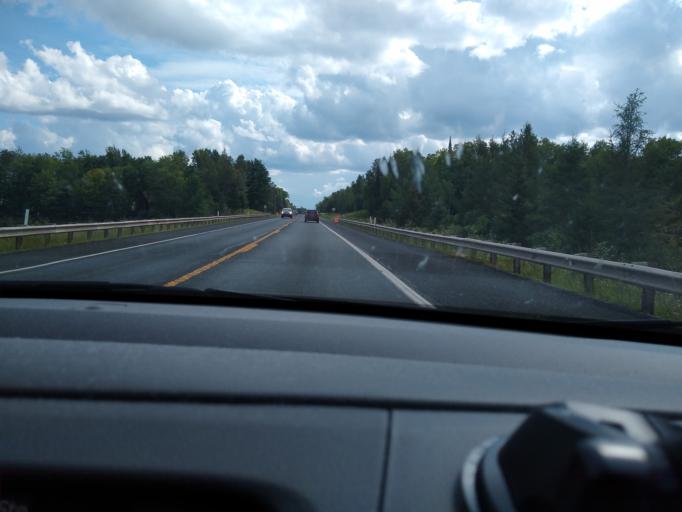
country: US
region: Michigan
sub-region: Iron County
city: Crystal Falls
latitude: 46.2802
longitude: -88.0178
